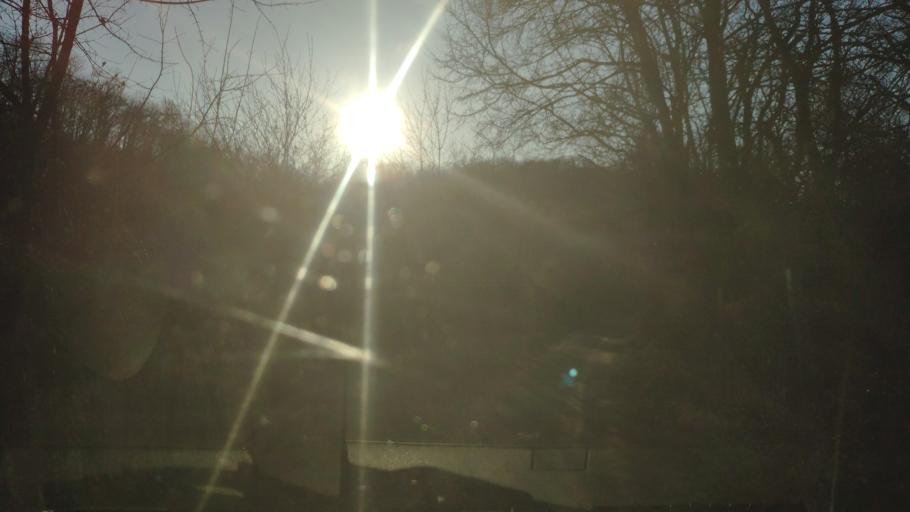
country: HU
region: Borsod-Abauj-Zemplen
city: Putnok
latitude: 48.5148
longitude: 20.3277
